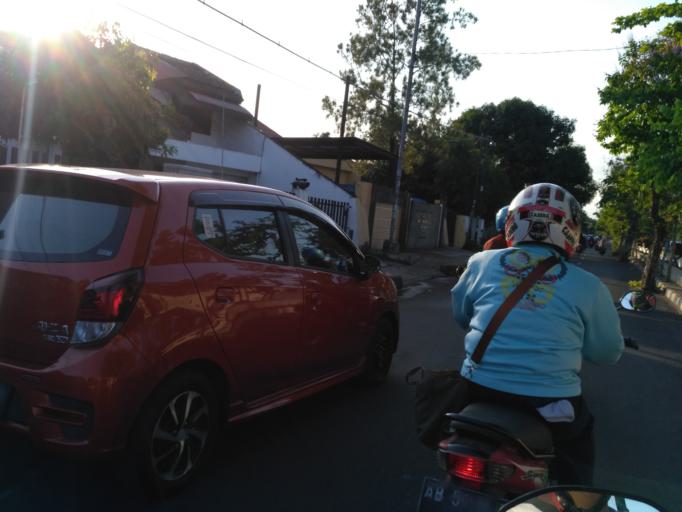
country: ID
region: Daerah Istimewa Yogyakarta
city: Yogyakarta
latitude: -7.8122
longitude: 110.3828
